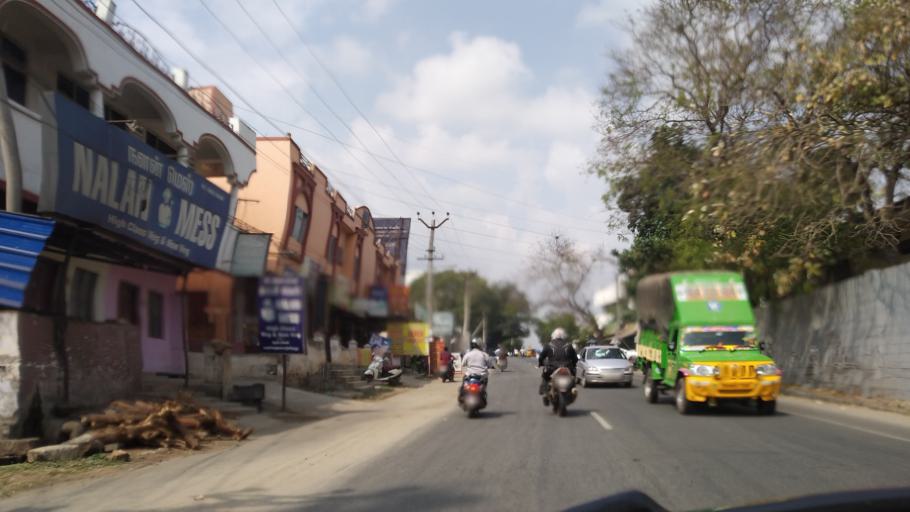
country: IN
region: Tamil Nadu
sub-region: Coimbatore
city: Madukkarai
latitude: 10.9394
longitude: 76.9477
